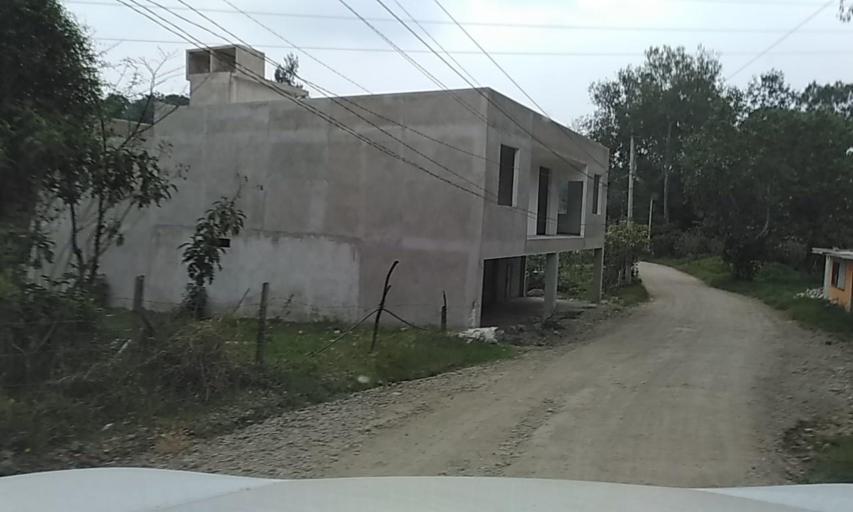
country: MX
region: Veracruz
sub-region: Jilotepec
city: El Pueblito (Garbanzal)
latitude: 19.5724
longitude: -96.8958
